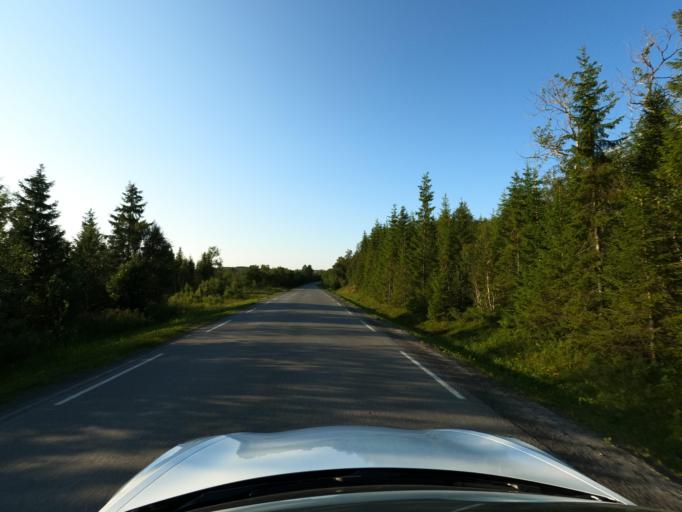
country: NO
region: Troms
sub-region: Skanland
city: Evenskjer
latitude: 68.4839
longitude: 16.7116
